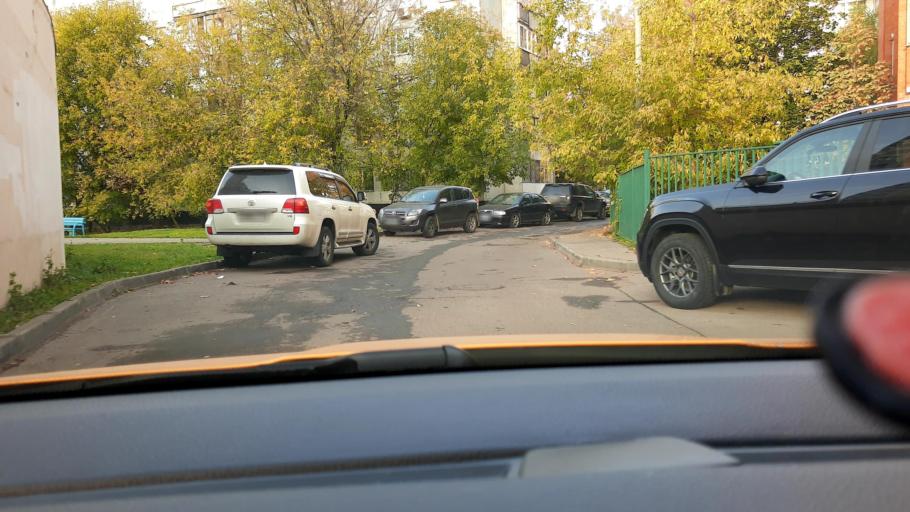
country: RU
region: Moscow
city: Businovo
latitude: 55.8780
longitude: 37.5160
